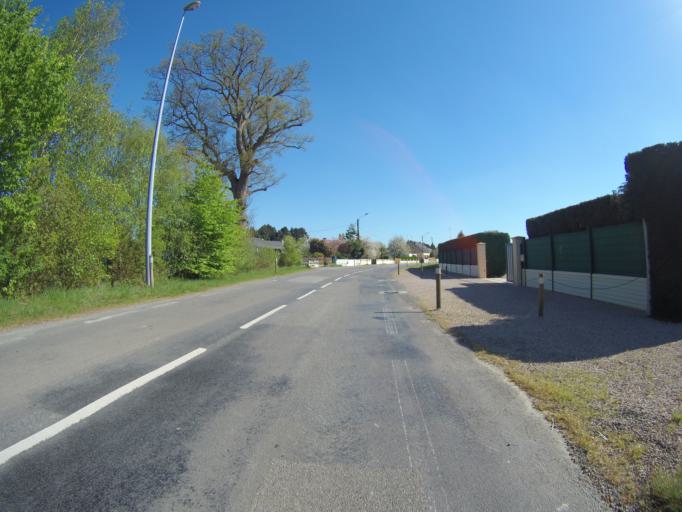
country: FR
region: Brittany
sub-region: Departement d'Ille-et-Vilaine
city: Chantepie
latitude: 48.0760
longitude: -1.6313
